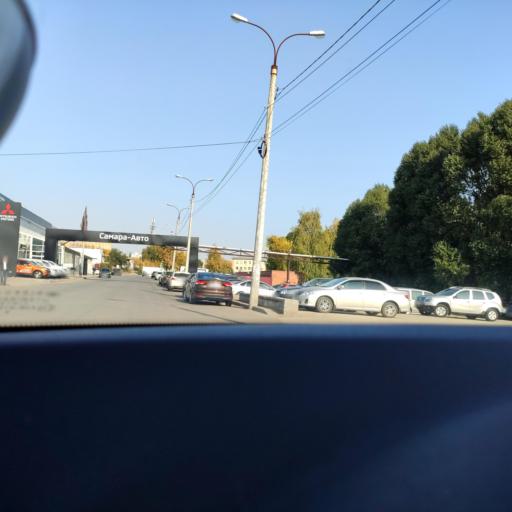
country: RU
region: Samara
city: Samara
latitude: 53.2387
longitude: 50.2474
